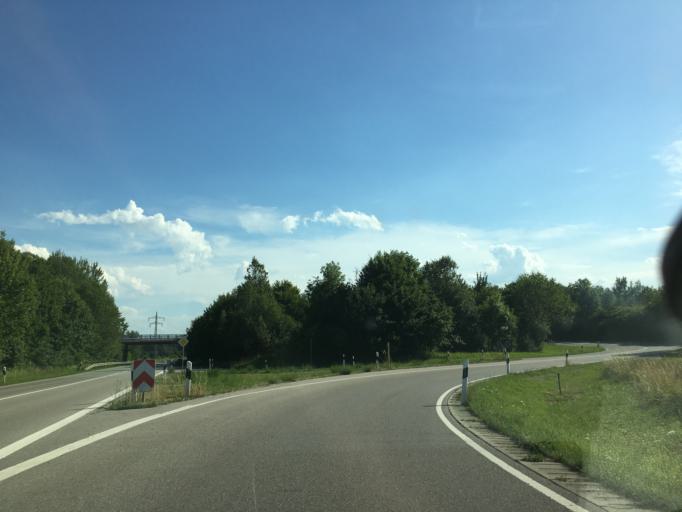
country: DE
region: Bavaria
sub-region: Upper Bavaria
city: Stammham
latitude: 48.2879
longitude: 11.8666
